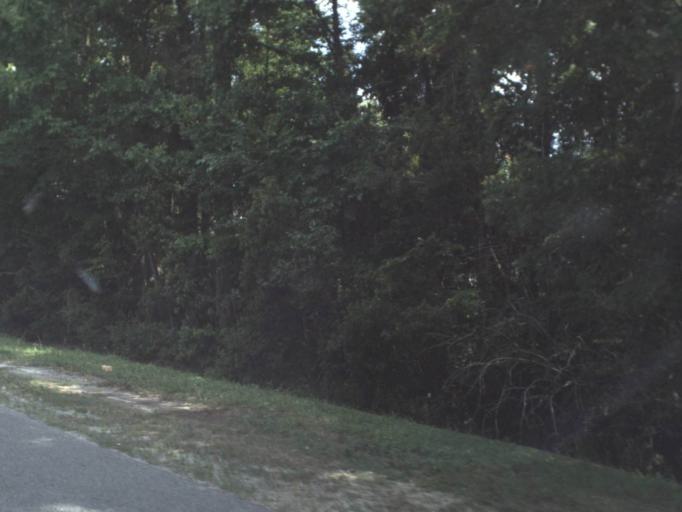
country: US
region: Florida
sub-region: Saint Johns County
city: Fruit Cove
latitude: 30.1985
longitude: -81.5717
